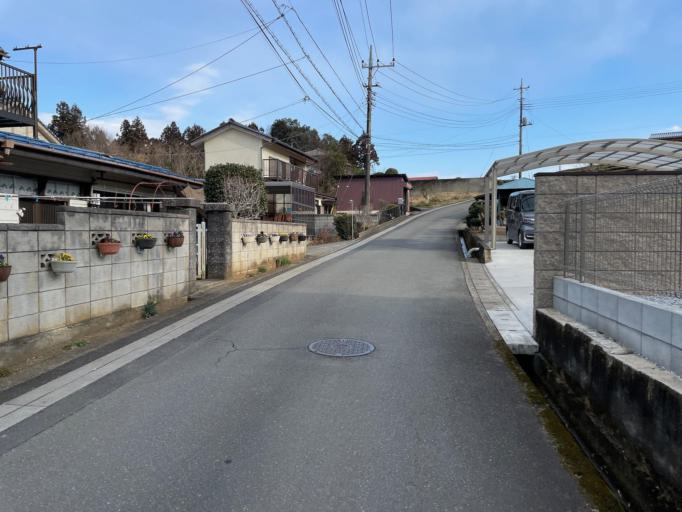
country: JP
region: Saitama
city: Hanno
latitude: 35.8358
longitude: 139.3166
